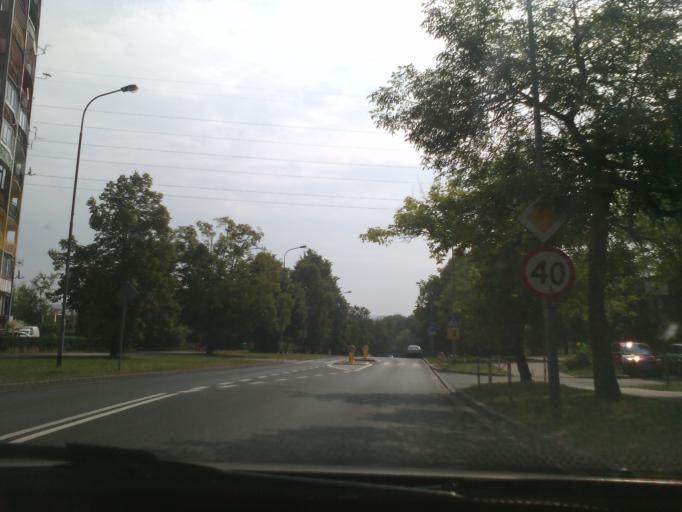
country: PL
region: Lower Silesian Voivodeship
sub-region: Powiat walbrzyski
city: Szczawno-Zdroj
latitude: 50.8086
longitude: 16.2851
